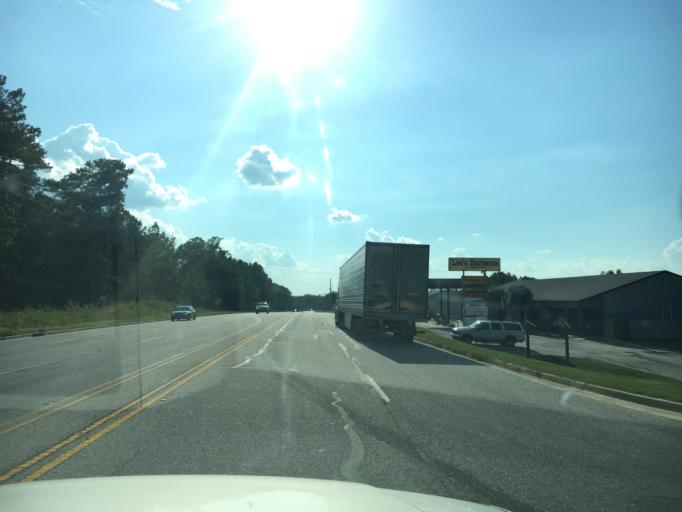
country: US
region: South Carolina
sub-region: Greenwood County
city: Ninety Six
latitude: 34.2872
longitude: -82.0469
